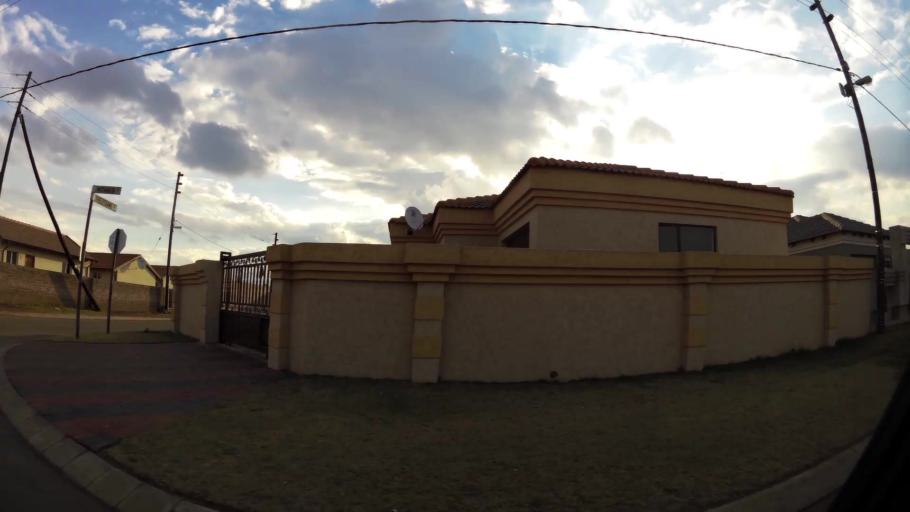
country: ZA
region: Gauteng
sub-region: Sedibeng District Municipality
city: Vanderbijlpark
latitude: -26.6090
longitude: 27.8130
